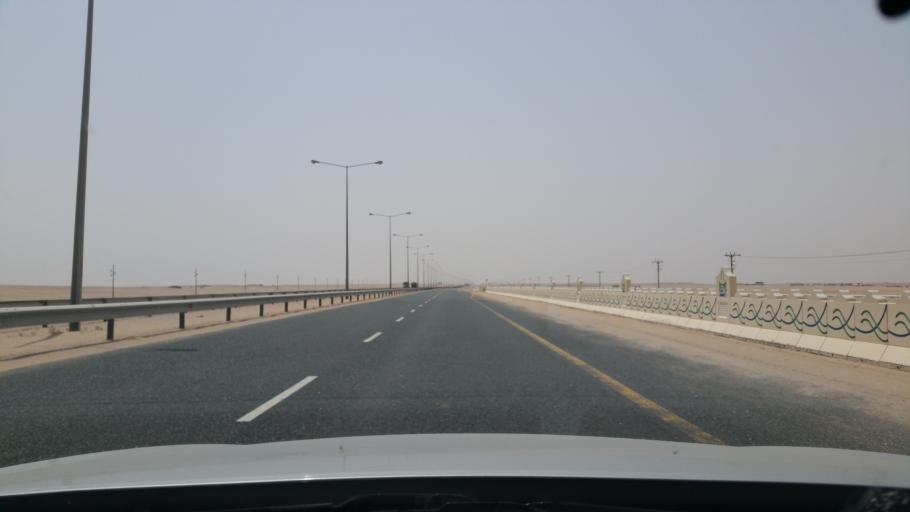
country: QA
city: Umm Bab
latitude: 25.0479
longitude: 50.8895
